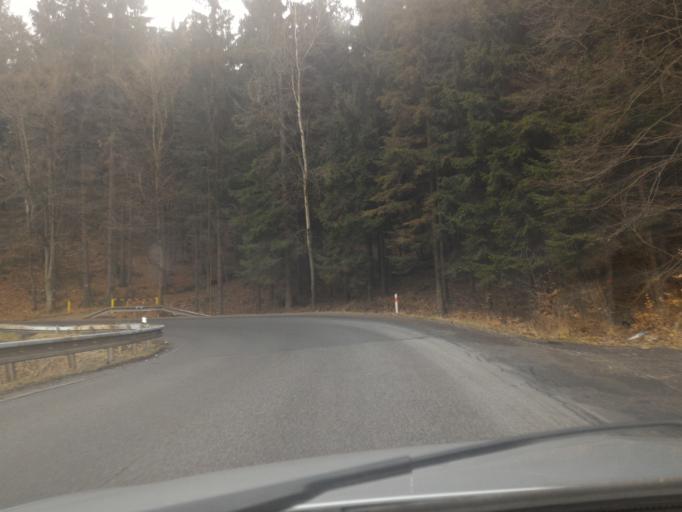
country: CZ
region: Liberecky
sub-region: Okres Jablonec nad Nisou
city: Janov nad Nisou
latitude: 50.7496
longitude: 15.1196
